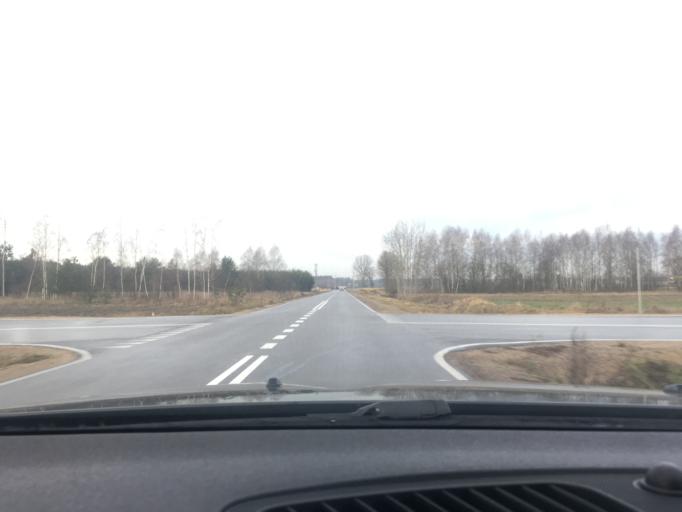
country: PL
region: Swietokrzyskie
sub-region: Powiat jedrzejowski
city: Jedrzejow
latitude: 50.6927
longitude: 20.3668
